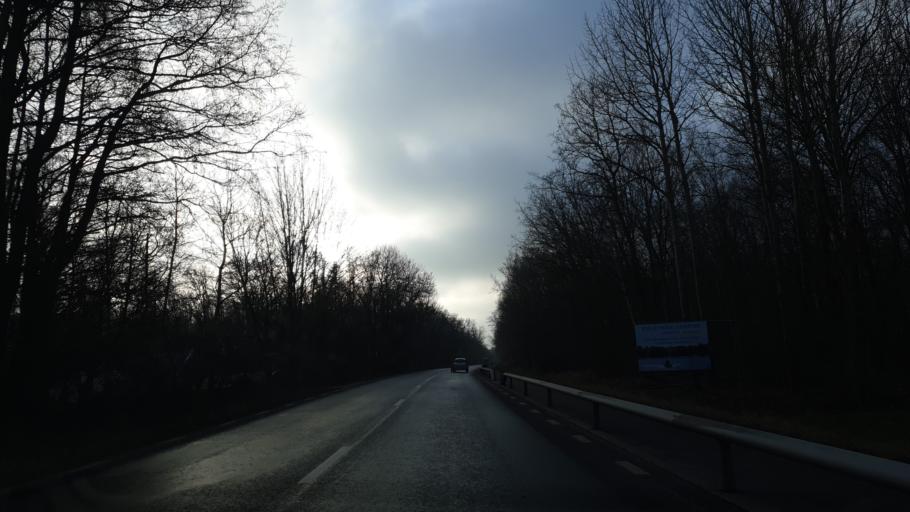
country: SE
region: Blekinge
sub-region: Karlshamns Kommun
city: Morrum
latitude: 56.1331
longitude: 14.6725
